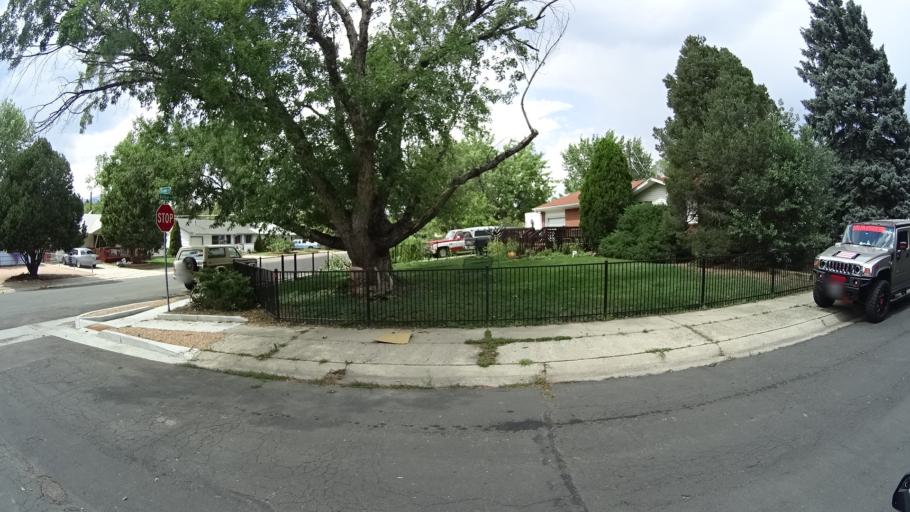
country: US
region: Colorado
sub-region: El Paso County
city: Colorado Springs
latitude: 38.8343
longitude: -104.7804
